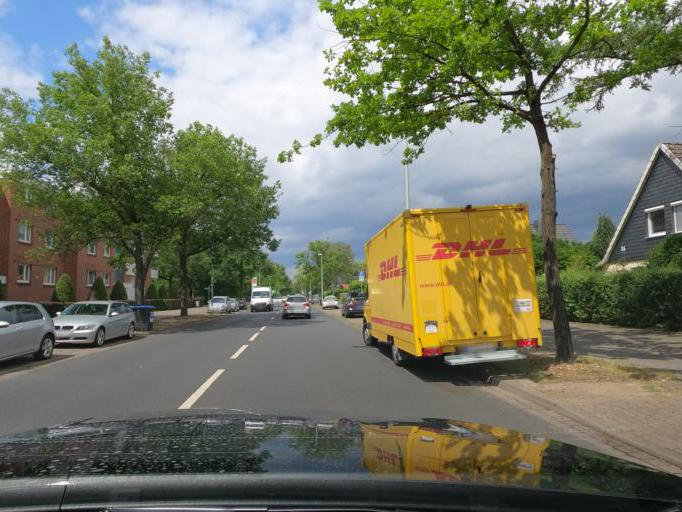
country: DE
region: Lower Saxony
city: Laatzen
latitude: 52.3886
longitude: 9.8205
